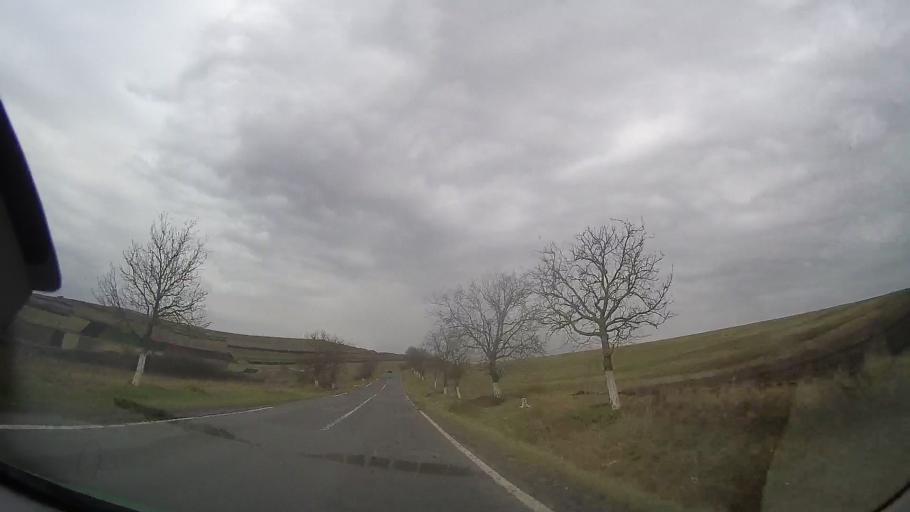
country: RO
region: Mures
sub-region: Comuna Faragau
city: Faragau
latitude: 46.7600
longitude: 24.5322
